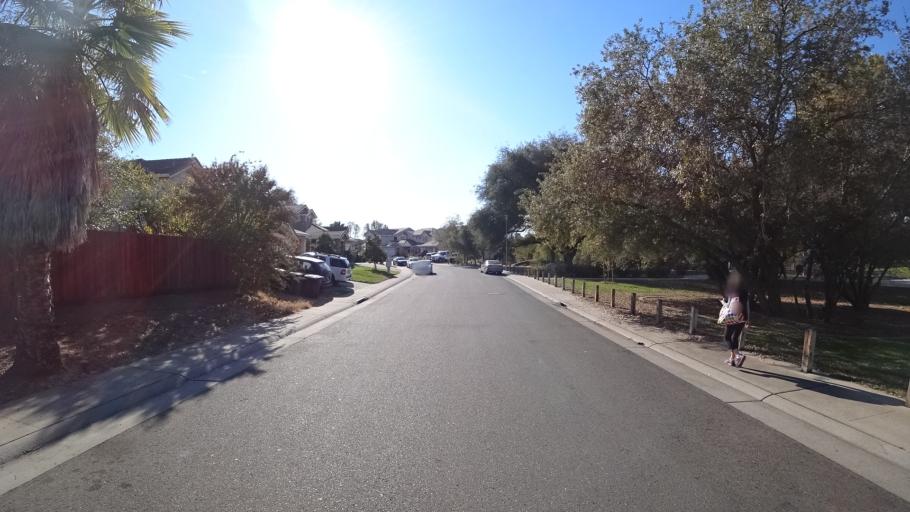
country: US
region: California
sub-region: Sacramento County
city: Citrus Heights
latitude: 38.6864
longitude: -121.2958
